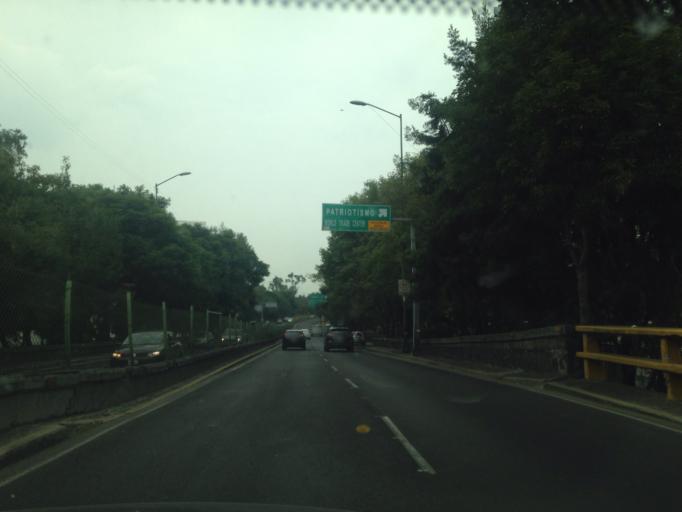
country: MX
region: Mexico City
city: Colonia del Valle
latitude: 19.3915
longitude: -99.1813
